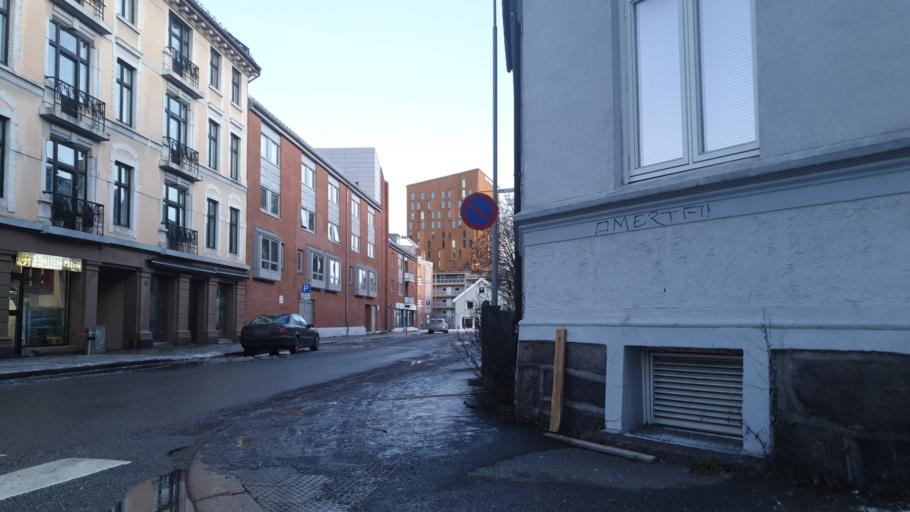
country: NO
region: Buskerud
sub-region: Drammen
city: Drammen
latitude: 59.7373
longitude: 10.2050
